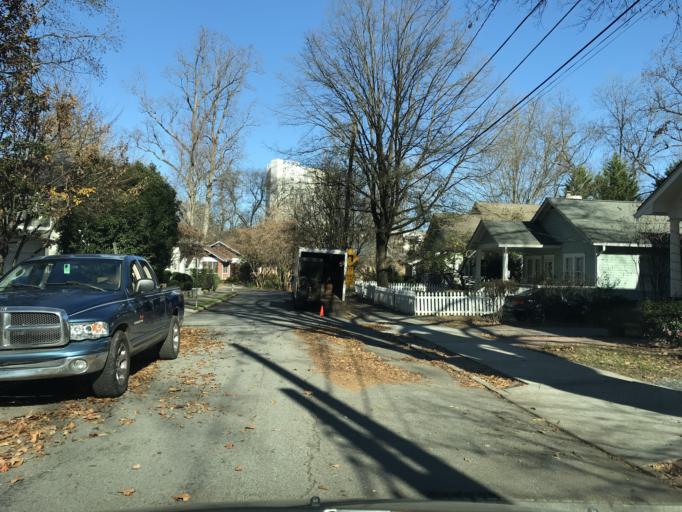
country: US
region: Georgia
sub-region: DeKalb County
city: Druid Hills
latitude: 33.7784
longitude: -84.3683
